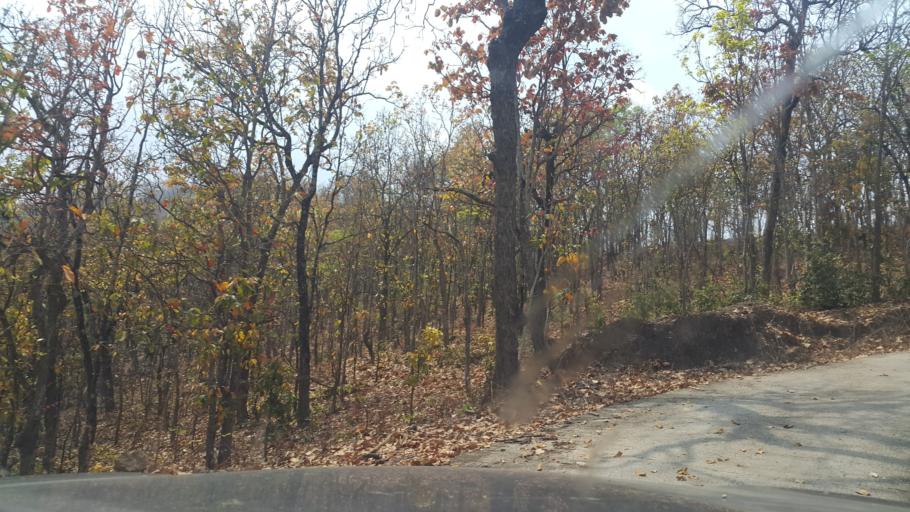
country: TH
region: Lamphun
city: Ban Hong
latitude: 18.2382
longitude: 98.8211
